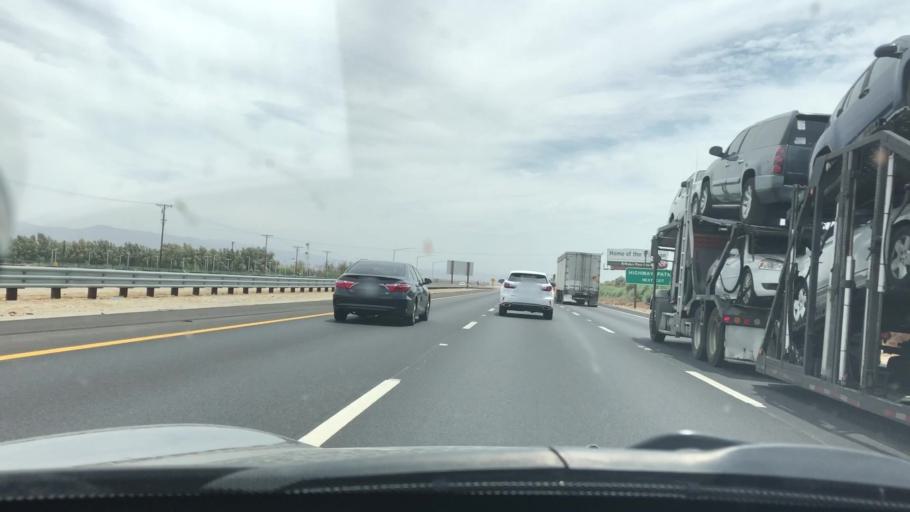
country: US
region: California
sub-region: Riverside County
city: Bermuda Dunes
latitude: 33.7535
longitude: -116.2821
